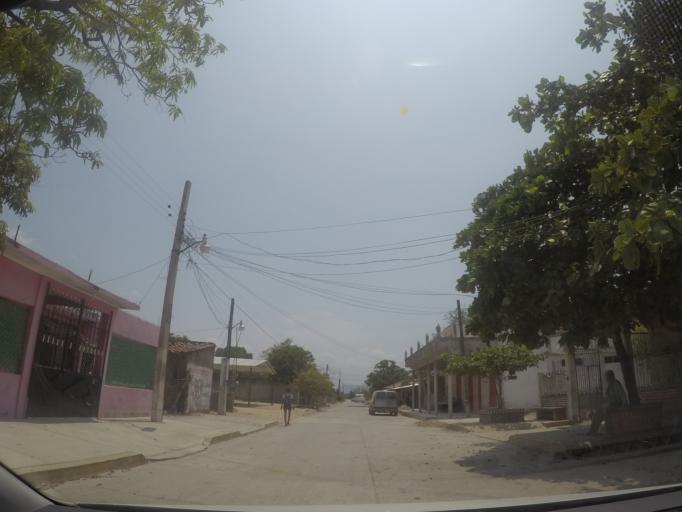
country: MX
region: Oaxaca
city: Asuncion Ixtaltepec
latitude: 16.5060
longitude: -95.0643
